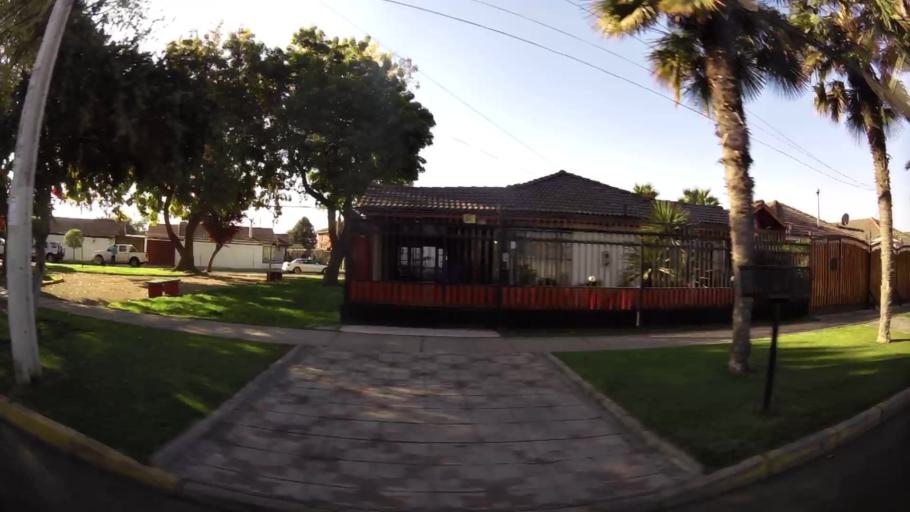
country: CL
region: Santiago Metropolitan
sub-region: Provincia de Santiago
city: Lo Prado
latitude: -33.4867
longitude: -70.7615
